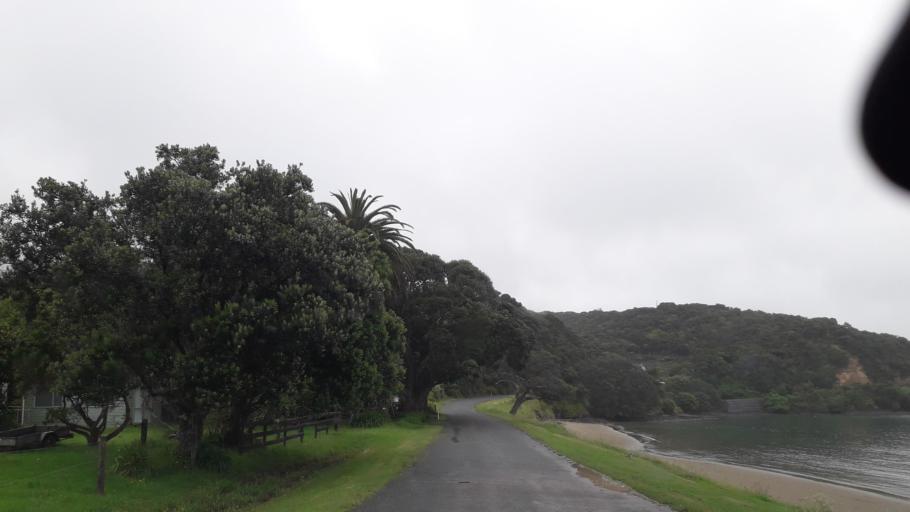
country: NZ
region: Northland
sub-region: Far North District
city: Paihia
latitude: -35.2256
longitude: 174.2633
